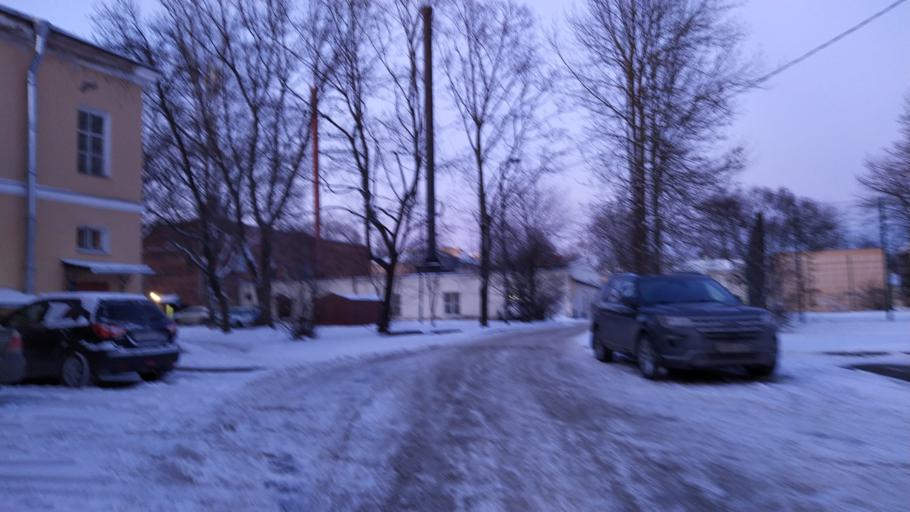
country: RU
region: St.-Petersburg
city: Pushkin
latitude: 59.7172
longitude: 30.4078
